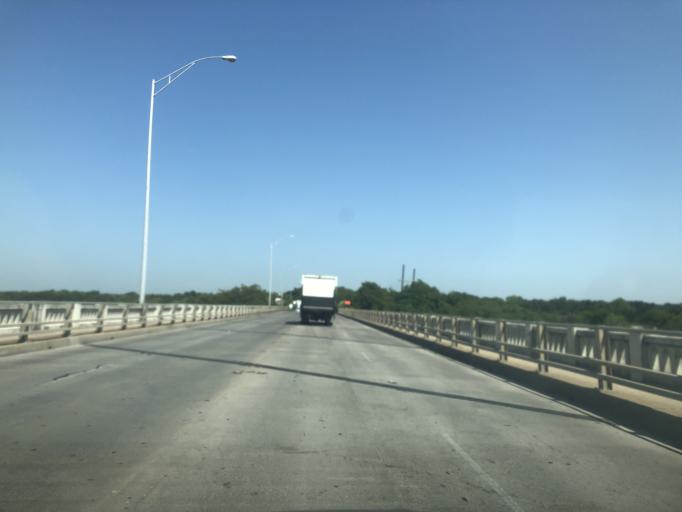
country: US
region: Texas
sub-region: Tarrant County
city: River Oaks
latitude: 32.7646
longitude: -97.3506
